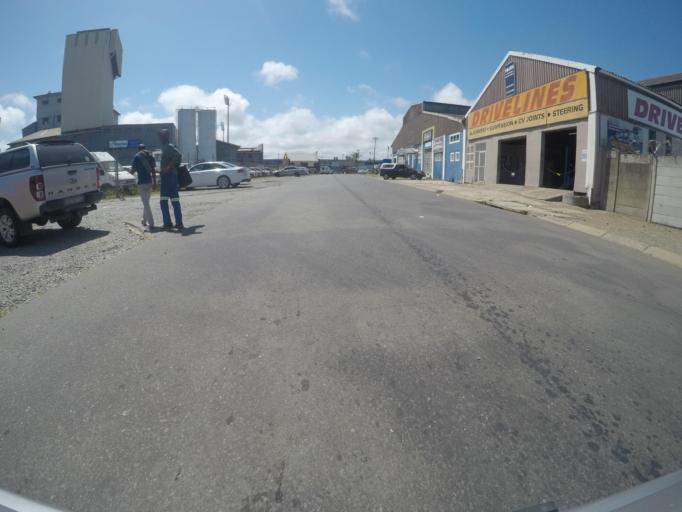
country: ZA
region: Eastern Cape
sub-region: Buffalo City Metropolitan Municipality
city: East London
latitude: -33.0096
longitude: 27.9094
